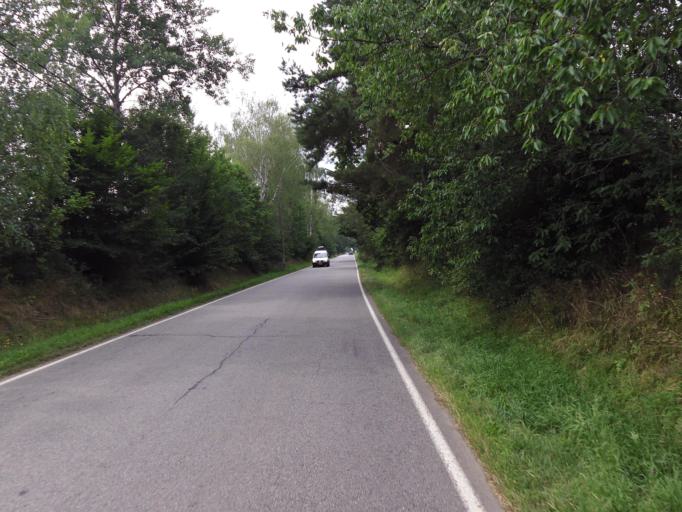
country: CZ
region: Central Bohemia
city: Kamenice
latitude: 49.8741
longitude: 14.6187
